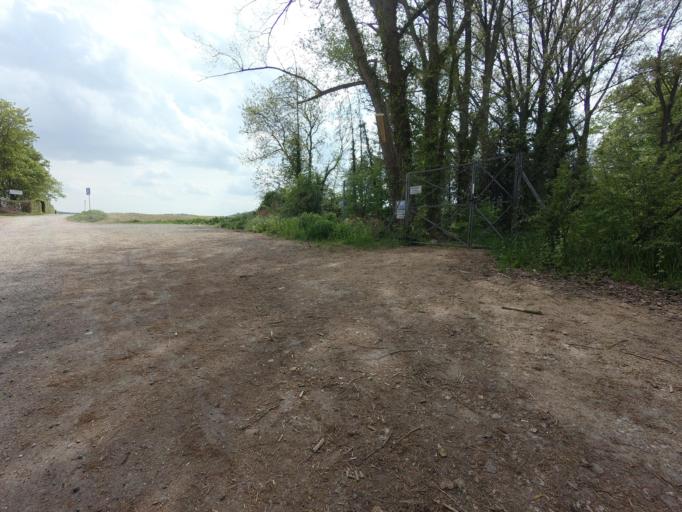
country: DE
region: Lower Saxony
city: Diekholzen
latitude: 52.1129
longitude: 9.9187
